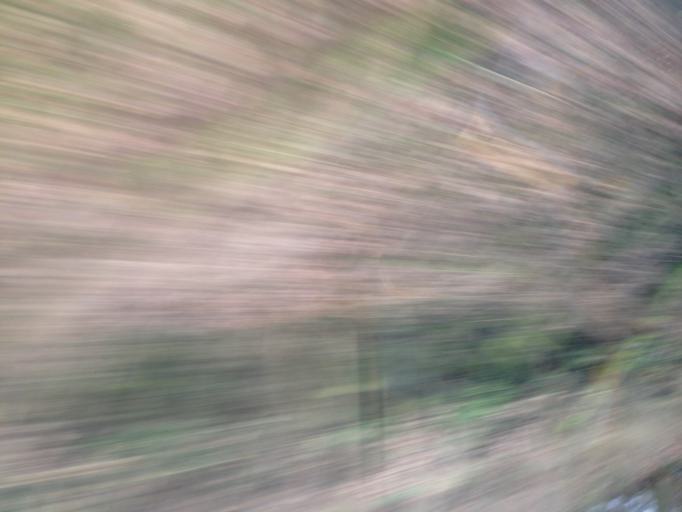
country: DE
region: Hesse
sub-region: Regierungsbezirk Giessen
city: Hungen
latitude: 50.4653
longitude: 8.9019
